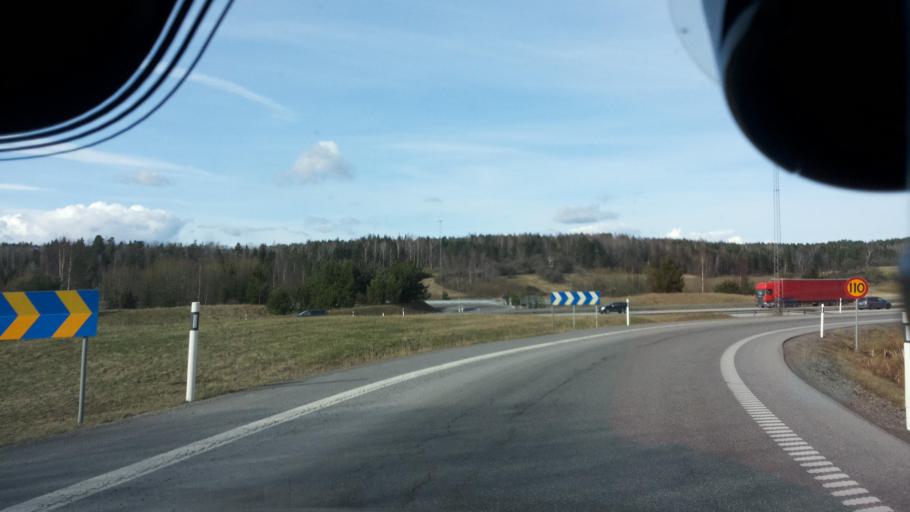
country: SE
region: Soedermanland
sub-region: Trosa Kommun
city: Vagnharad
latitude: 58.9608
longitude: 17.4869
